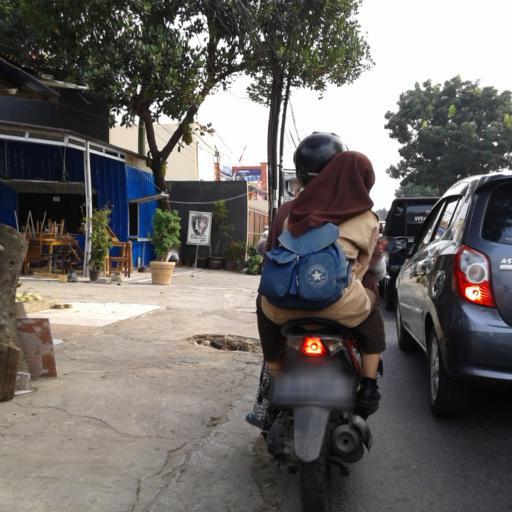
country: ID
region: West Java
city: Sawangan
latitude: -6.3687
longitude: 106.7742
